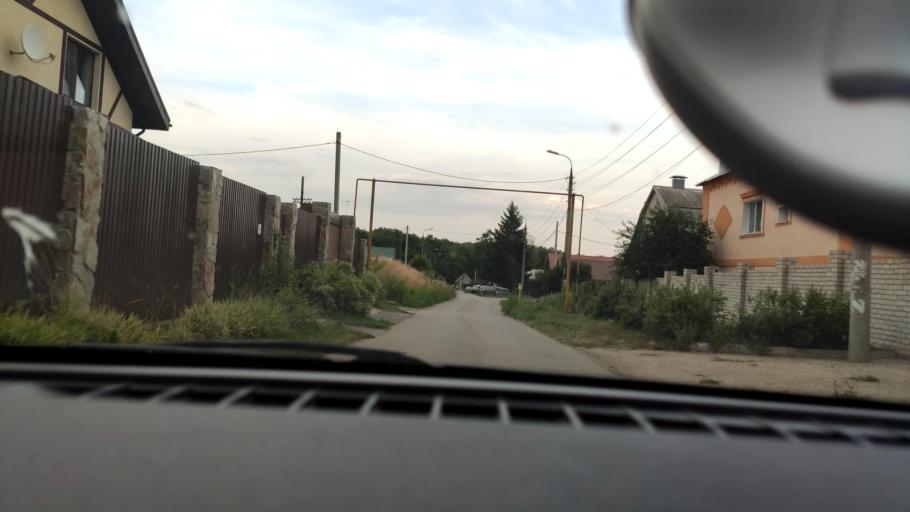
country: RU
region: Samara
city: Petra-Dubrava
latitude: 53.2954
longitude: 50.3717
